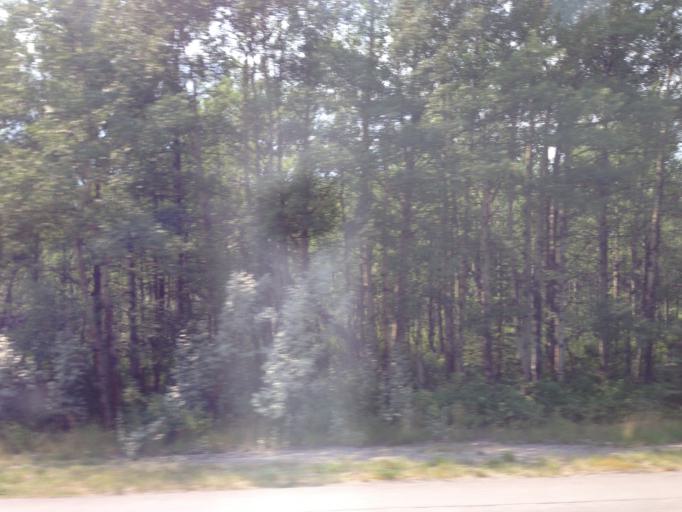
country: CA
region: Alberta
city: Canmore
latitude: 51.0776
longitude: -115.3386
